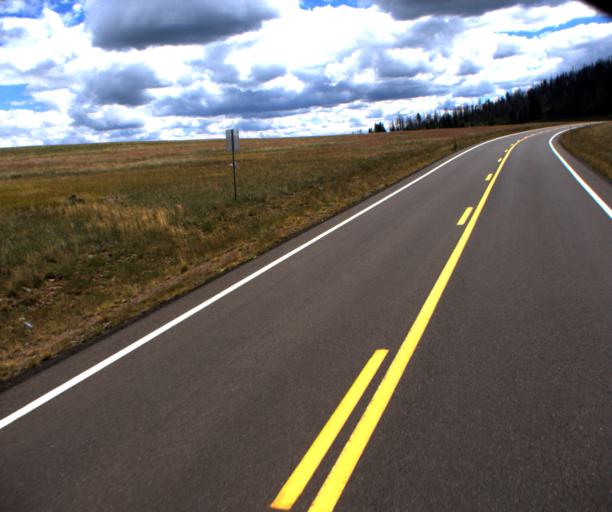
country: US
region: Arizona
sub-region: Apache County
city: Eagar
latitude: 33.9148
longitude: -109.4190
